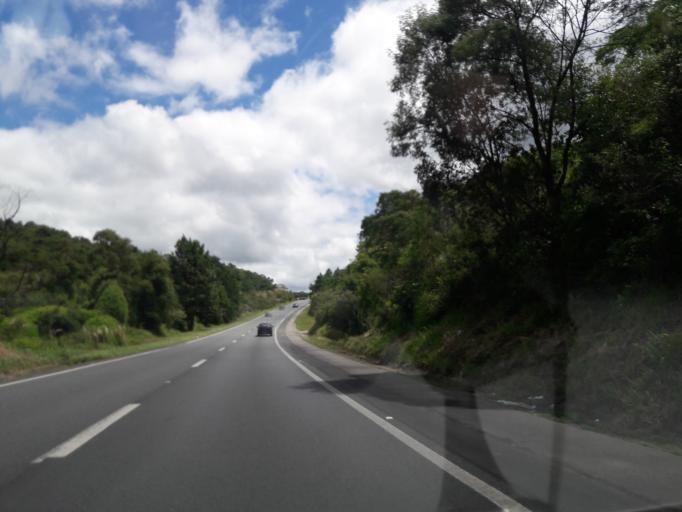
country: BR
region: Parana
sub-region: Campina Grande Do Sul
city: Campina Grande do Sul
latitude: -25.1034
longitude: -48.8085
